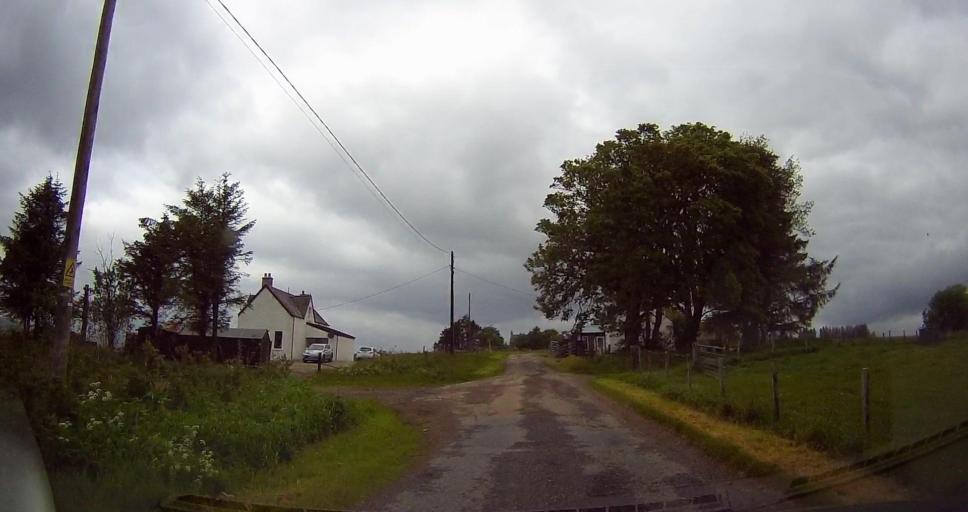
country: GB
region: Scotland
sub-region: Highland
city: Alness
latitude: 58.0716
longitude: -4.4340
